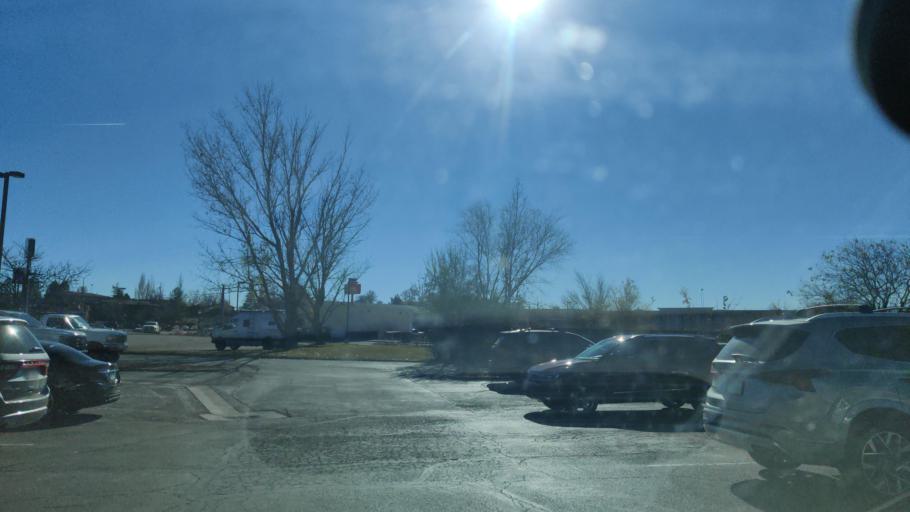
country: US
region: Colorado
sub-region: Mesa County
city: Grand Junction
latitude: 39.1120
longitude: -108.5419
